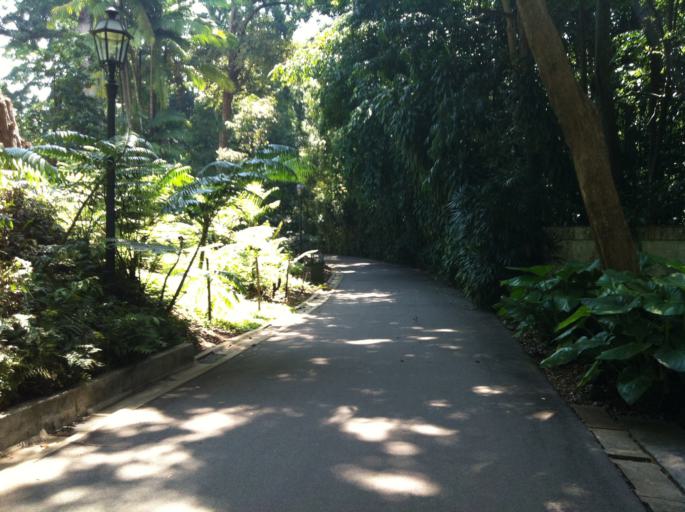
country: SG
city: Singapore
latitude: 1.3106
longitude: 103.8171
